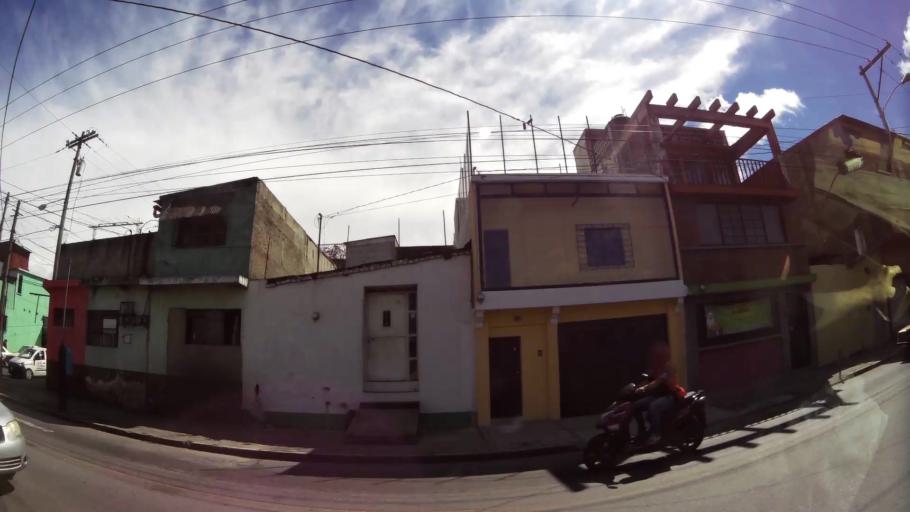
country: GT
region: Guatemala
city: Guatemala City
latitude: 14.6068
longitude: -90.5356
